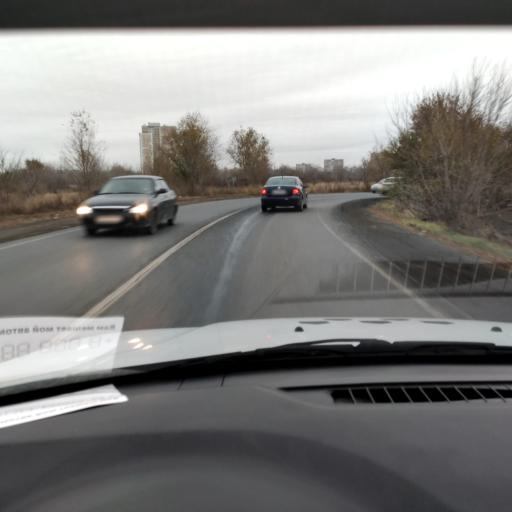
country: RU
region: Samara
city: Tol'yatti
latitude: 53.5142
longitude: 49.2447
